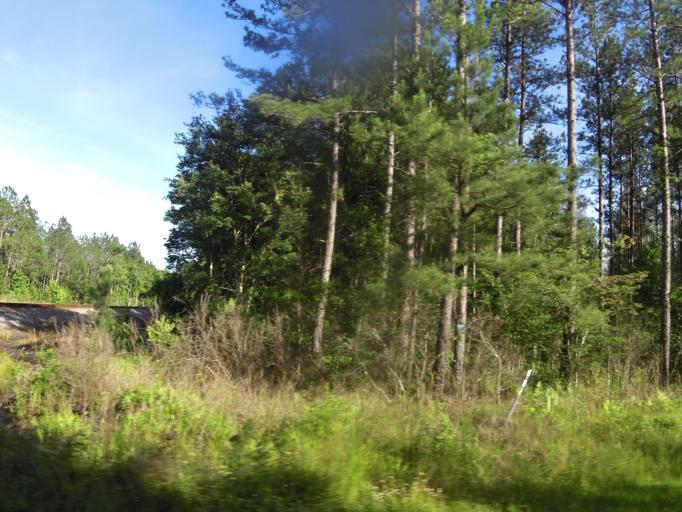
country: US
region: Florida
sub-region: Nassau County
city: Nassau Village-Ratliff
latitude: 30.4605
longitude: -81.8245
